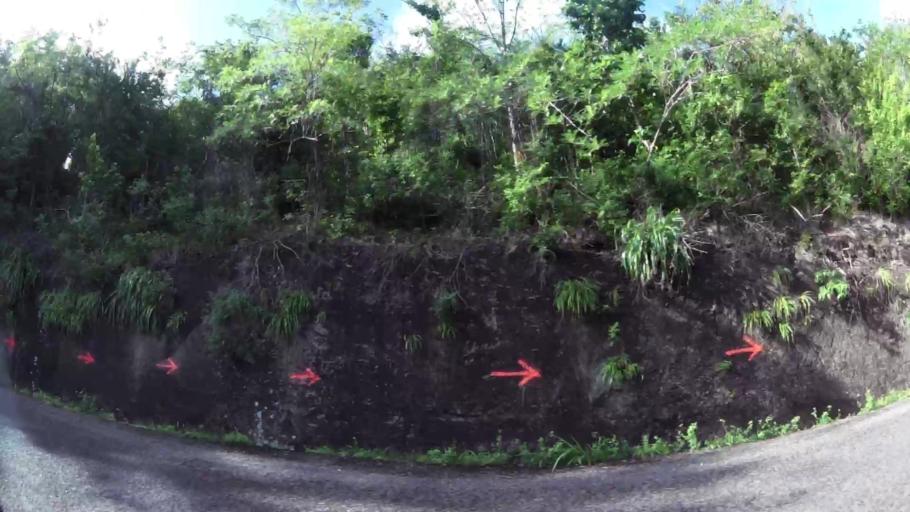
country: LC
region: Anse-la-Raye
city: Canaries
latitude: 13.9010
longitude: -61.0675
